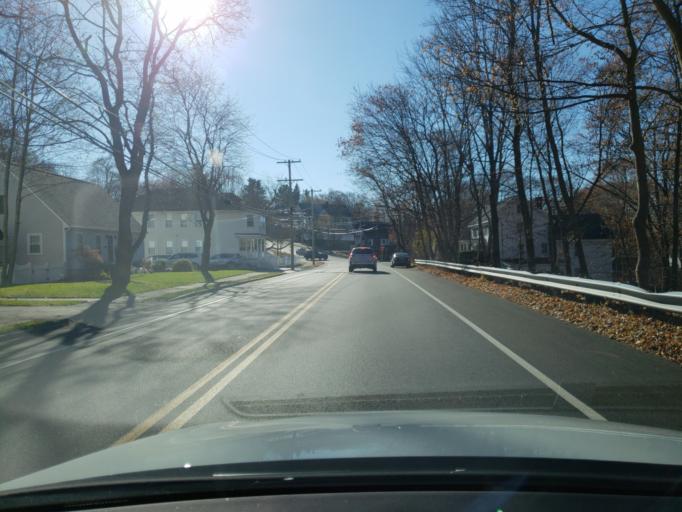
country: US
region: Massachusetts
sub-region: Essex County
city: Andover
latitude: 42.6634
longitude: -71.1417
